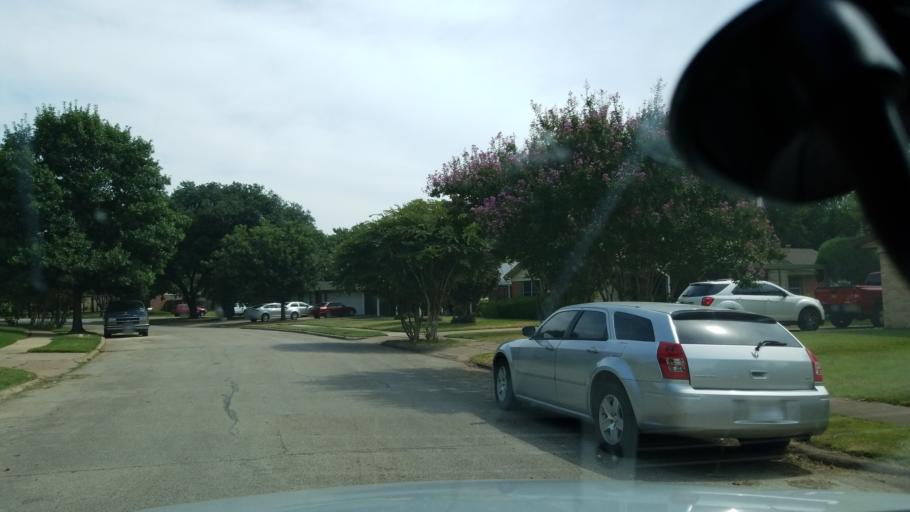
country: US
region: Texas
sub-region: Dallas County
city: Irving
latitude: 32.8250
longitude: -96.9794
